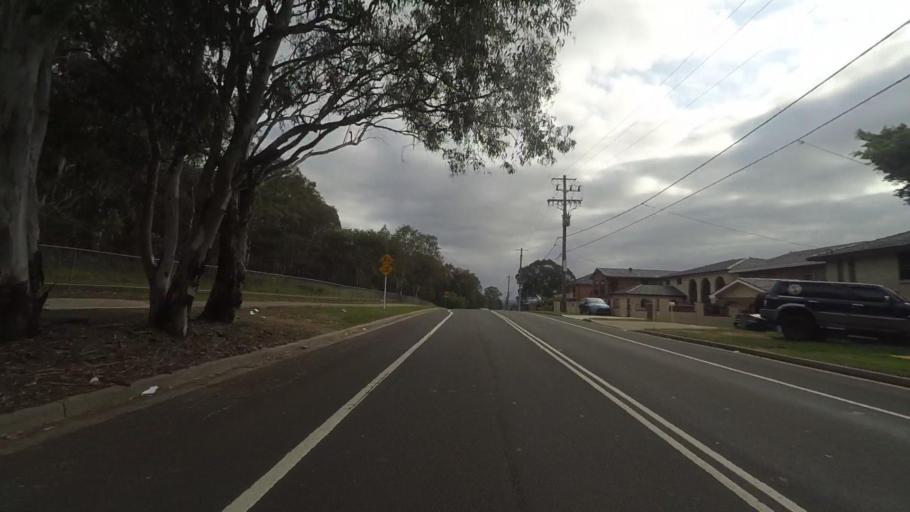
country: AU
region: New South Wales
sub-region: Bankstown
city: Regents Park
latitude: -33.9063
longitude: 150.9928
